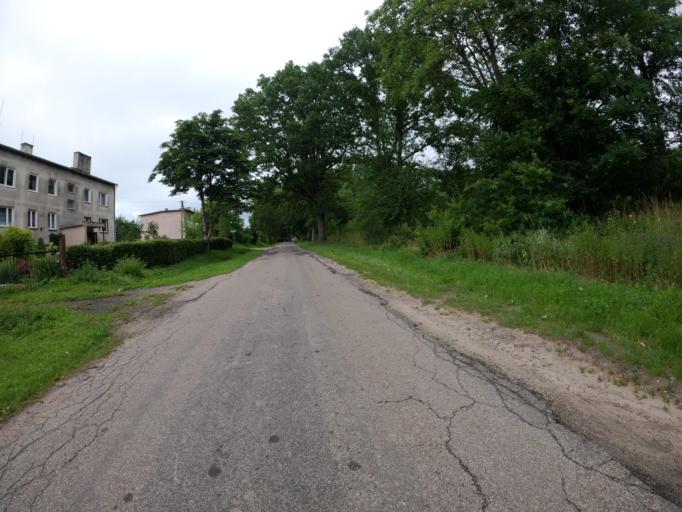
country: PL
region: West Pomeranian Voivodeship
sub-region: Powiat szczecinecki
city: Grzmiaca
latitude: 53.9340
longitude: 16.4546
